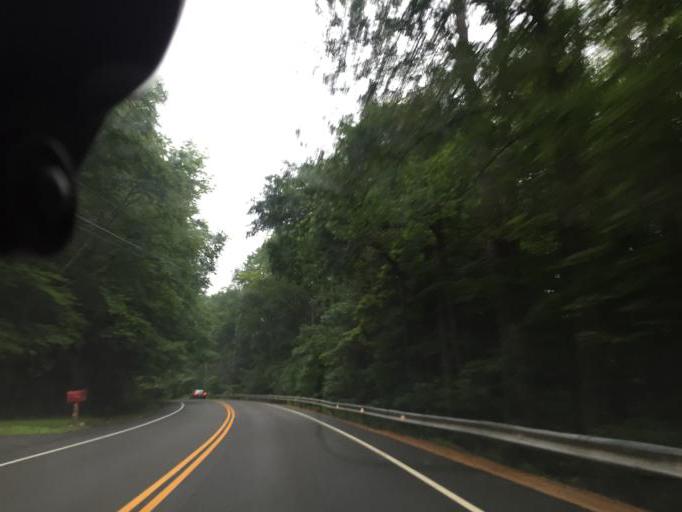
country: US
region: Connecticut
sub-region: Litchfield County
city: Canaan
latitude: 41.9065
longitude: -73.2727
